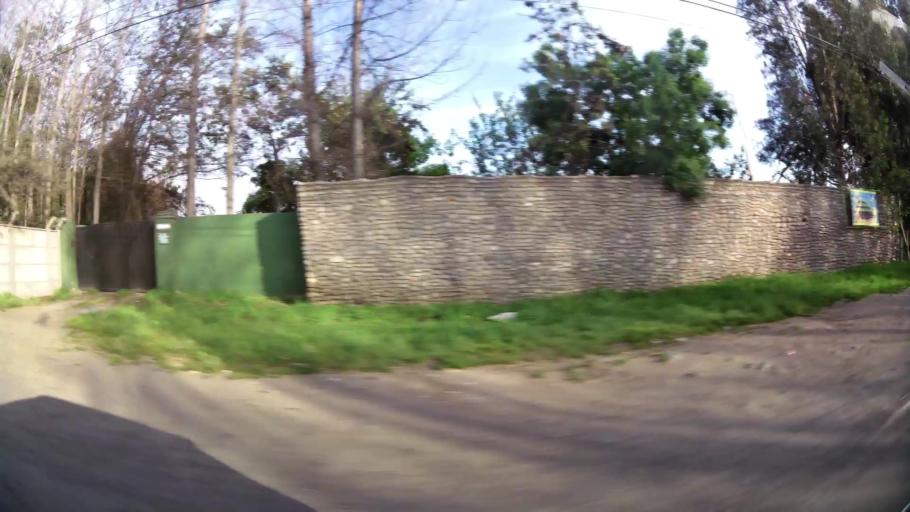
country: CL
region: Santiago Metropolitan
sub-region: Provincia de Maipo
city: San Bernardo
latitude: -33.5587
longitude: -70.7566
